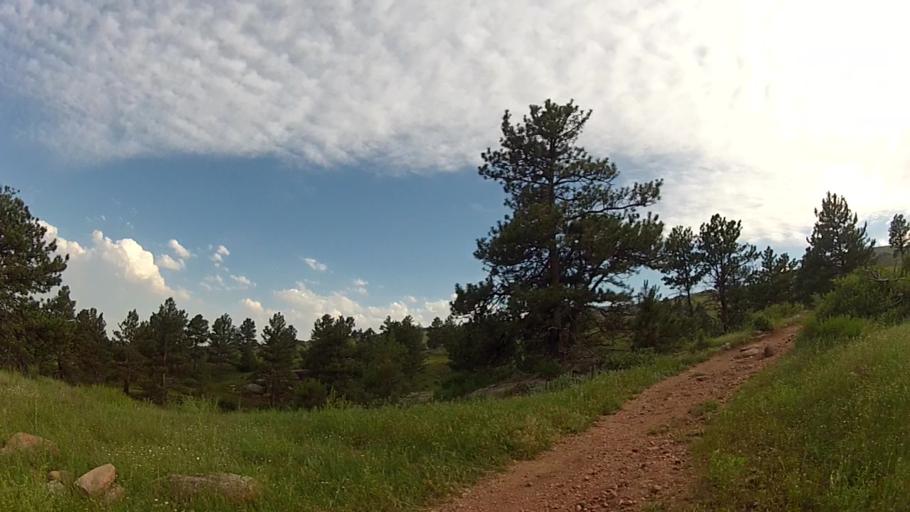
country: US
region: Colorado
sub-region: Larimer County
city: Loveland
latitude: 40.4750
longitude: -105.2330
